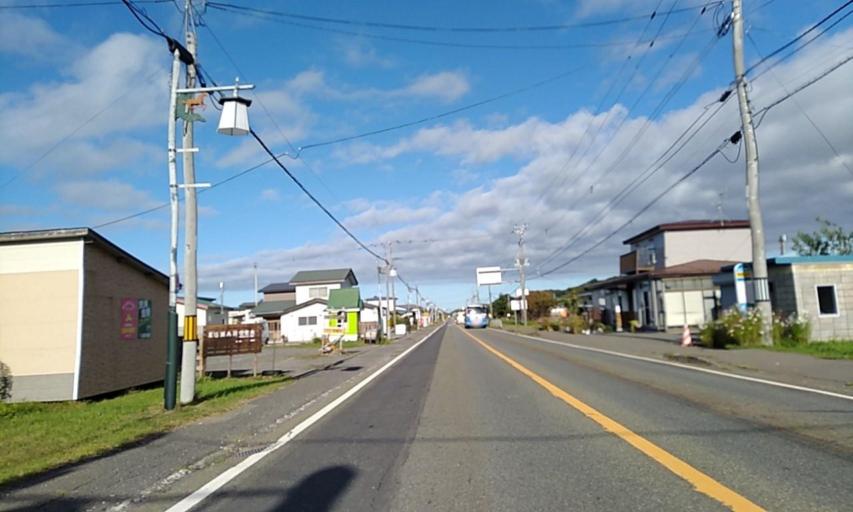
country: JP
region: Hokkaido
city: Shizunai-furukawacho
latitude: 42.2247
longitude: 142.6261
